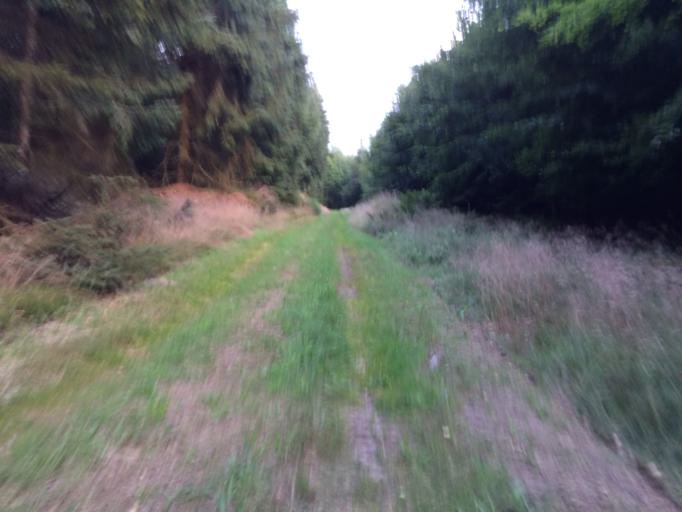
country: DK
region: Central Jutland
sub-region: Holstebro Kommune
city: Ulfborg
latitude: 56.2544
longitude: 8.3728
